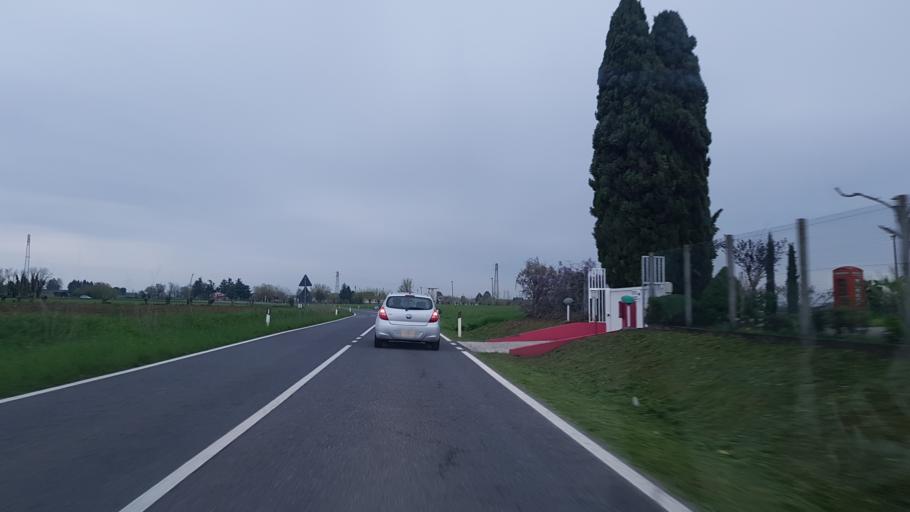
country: IT
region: Friuli Venezia Giulia
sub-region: Provincia di Udine
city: Sottoselva
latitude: 45.9000
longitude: 13.3232
